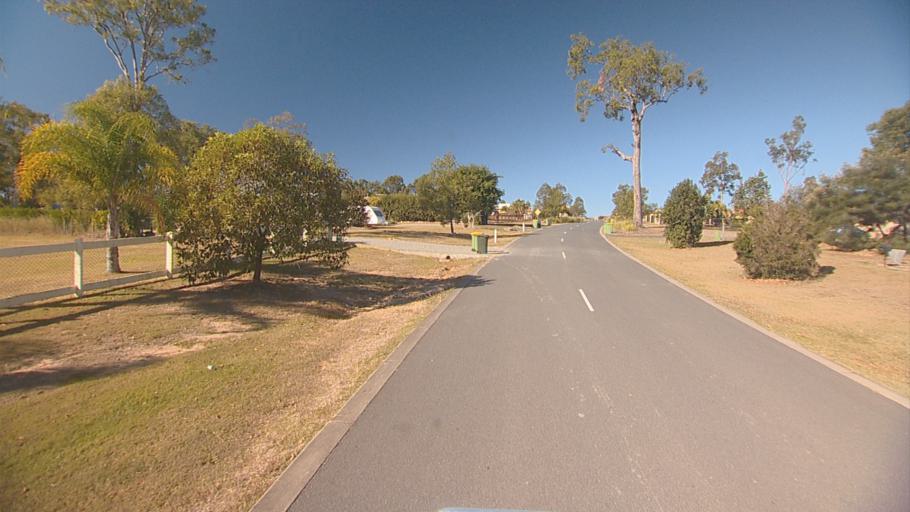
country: AU
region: Queensland
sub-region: Logan
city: North Maclean
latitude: -27.7532
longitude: 152.9565
